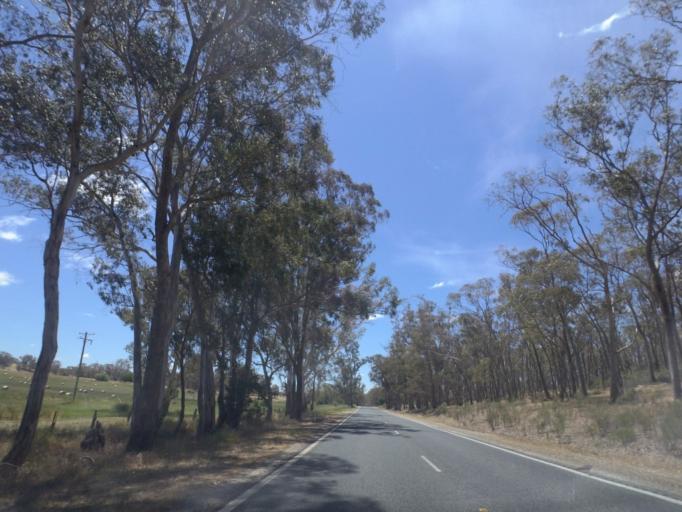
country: AU
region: Victoria
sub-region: Mount Alexander
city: Castlemaine
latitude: -37.1839
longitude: 144.1482
